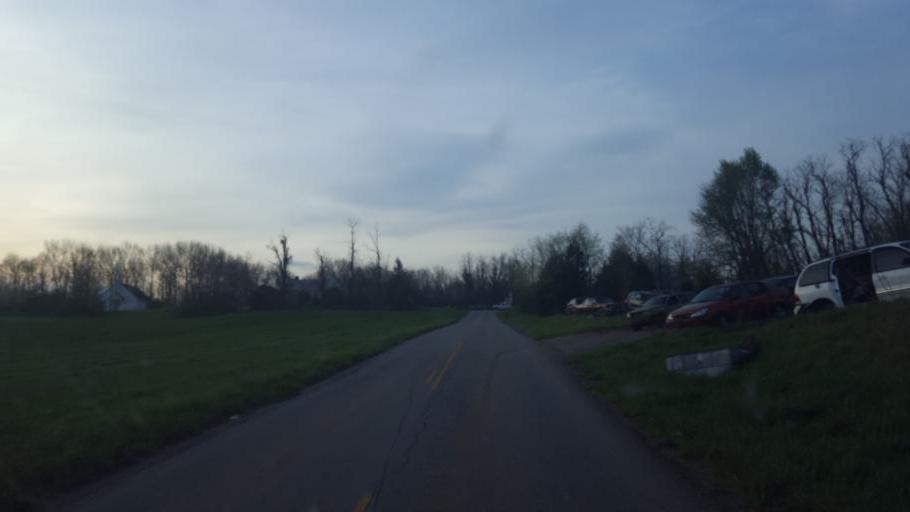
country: US
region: Kentucky
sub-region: Metcalfe County
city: Edmonton
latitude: 37.1393
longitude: -85.6946
